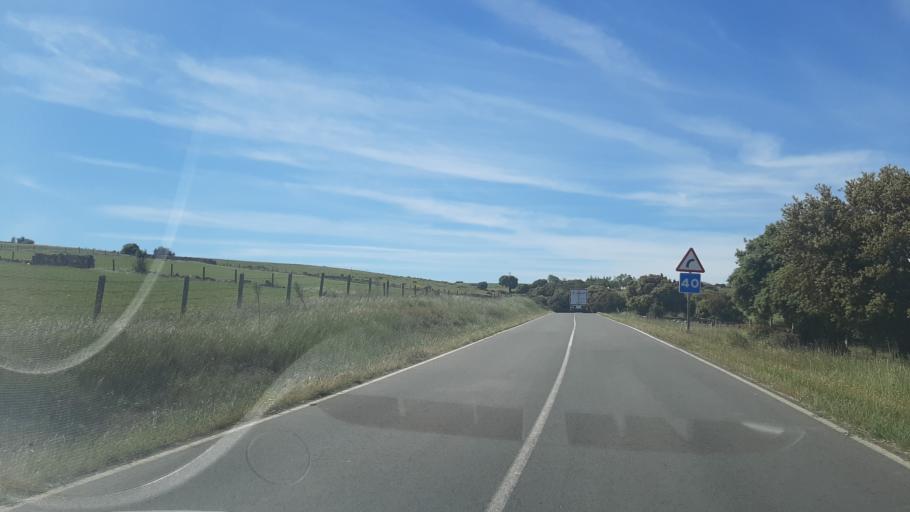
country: ES
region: Castille and Leon
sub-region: Provincia de Salamanca
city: Aldeavieja de Tormes
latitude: 40.5495
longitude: -5.5942
